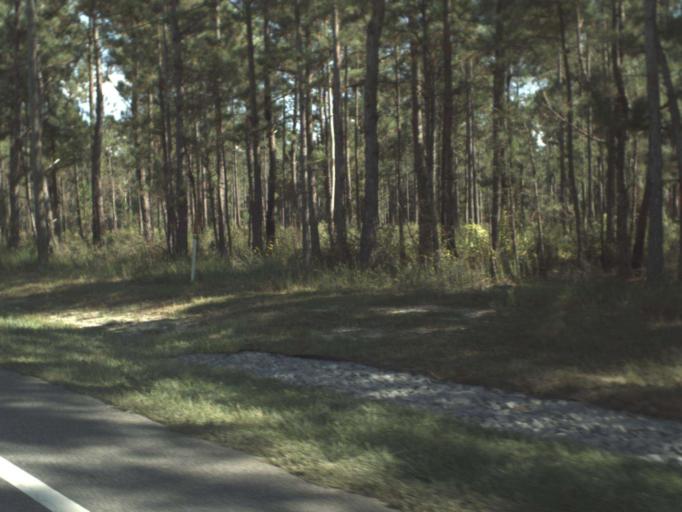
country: US
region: Florida
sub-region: Walton County
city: Freeport
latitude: 30.4783
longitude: -86.0631
